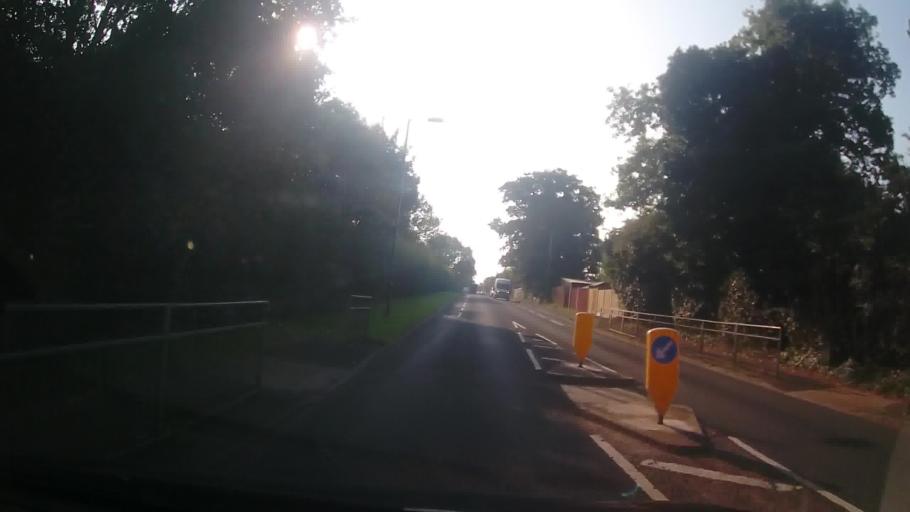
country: GB
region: England
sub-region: Shropshire
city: Astley
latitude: 52.7317
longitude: -2.7137
